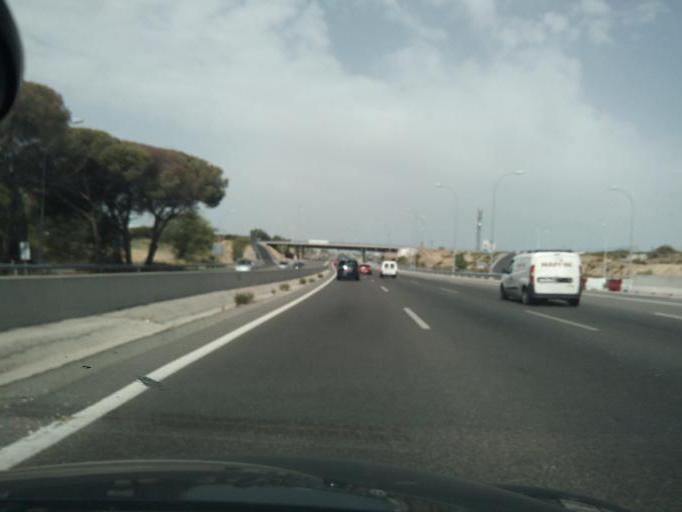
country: ES
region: Madrid
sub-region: Provincia de Madrid
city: Barajas de Madrid
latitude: 40.4719
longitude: -3.6084
